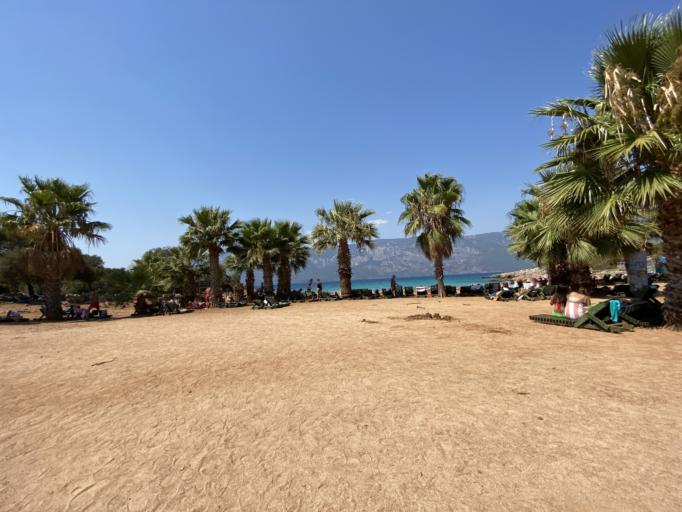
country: TR
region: Mugla
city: Yerkesik
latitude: 36.9927
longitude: 28.2036
